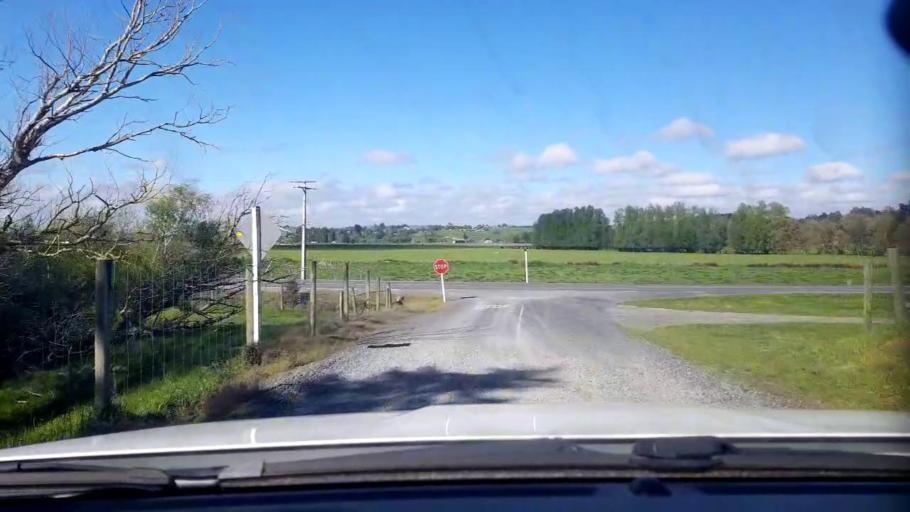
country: NZ
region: Otago
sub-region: Clutha District
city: Balclutha
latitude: -46.2235
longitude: 169.7323
